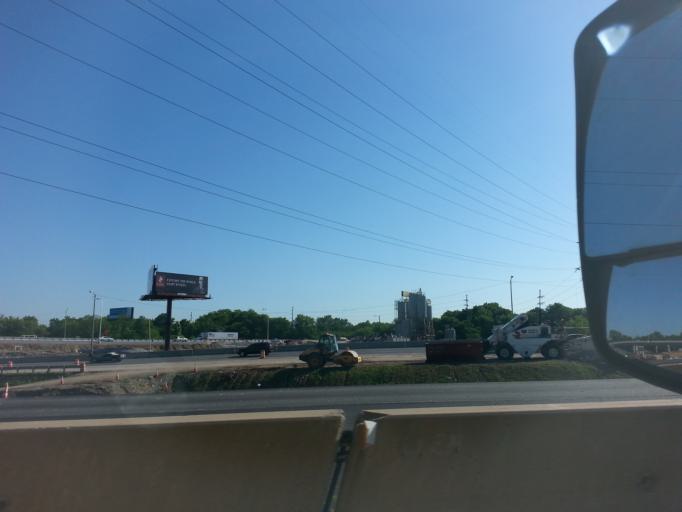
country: US
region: Indiana
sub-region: Clark County
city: Jeffersonville
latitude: 38.2604
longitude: -85.7256
